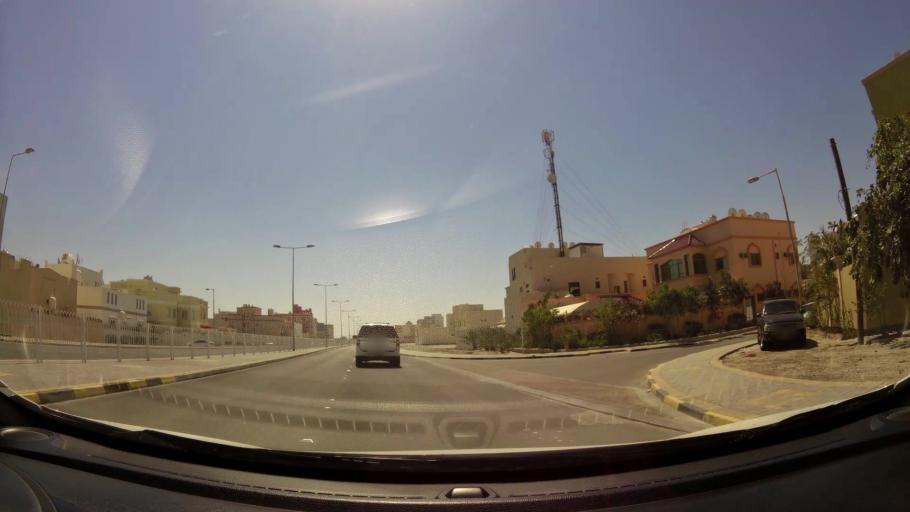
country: BH
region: Muharraq
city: Al Hadd
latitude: 26.2800
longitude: 50.6429
